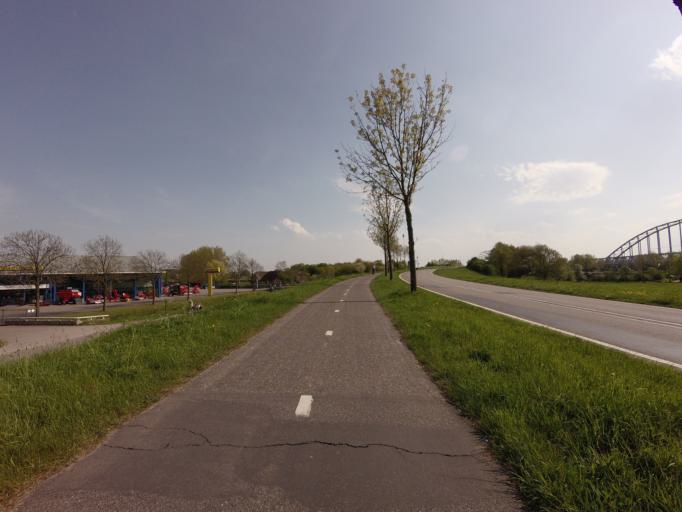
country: NL
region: Utrecht
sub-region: Gemeente Houten
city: Houten
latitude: 52.0088
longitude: 5.1873
